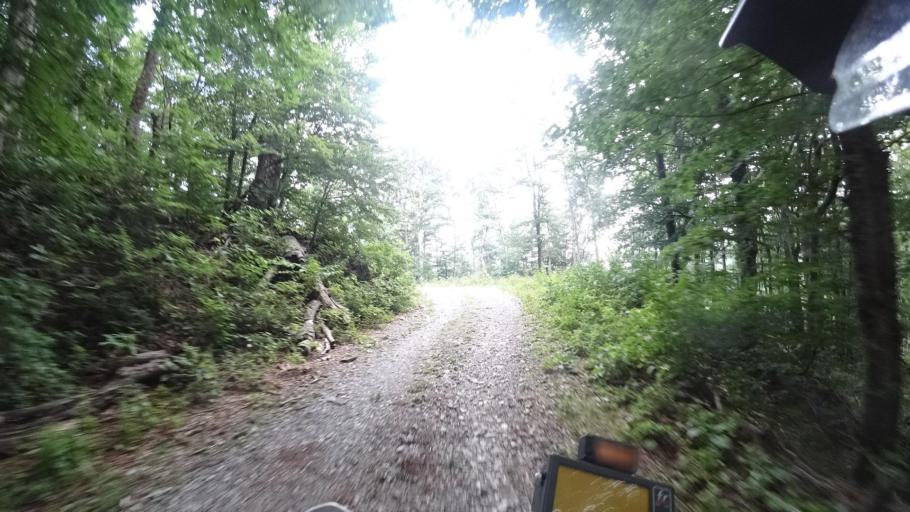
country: HR
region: Primorsko-Goranska
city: Novi Vinodolski
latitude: 45.1255
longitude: 14.9177
